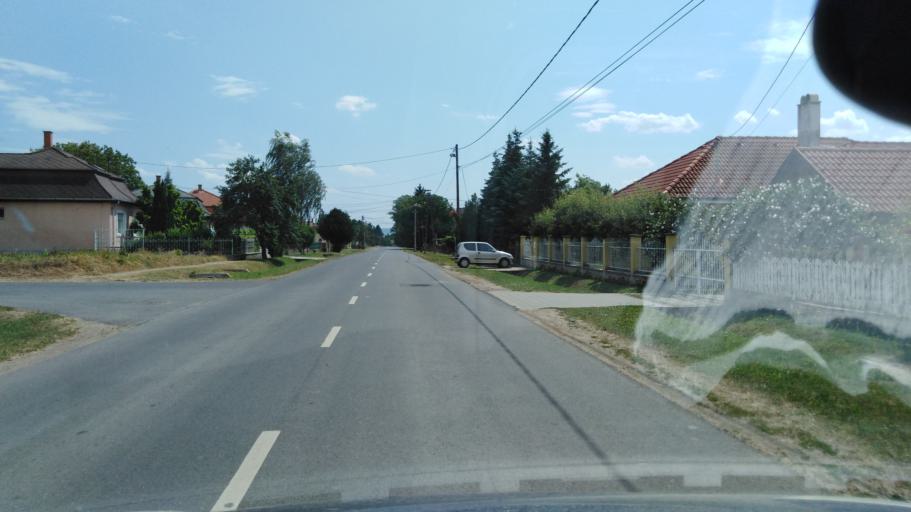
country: HU
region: Nograd
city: Szecseny
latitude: 48.1456
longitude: 19.5314
